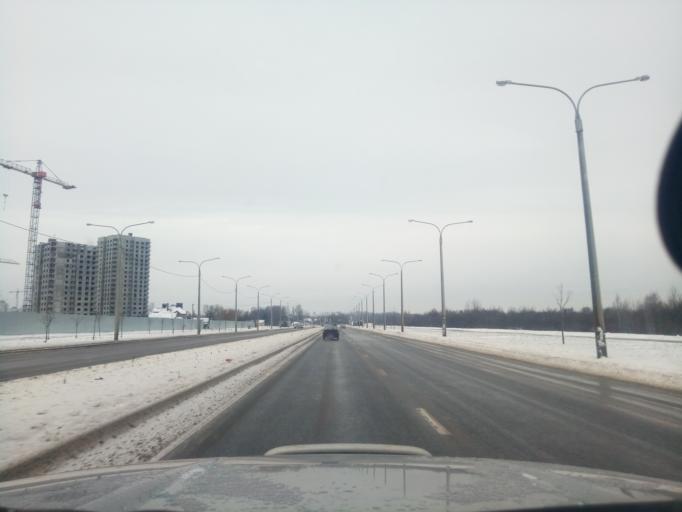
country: BY
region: Minsk
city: Machulishchy
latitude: 53.8381
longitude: 27.5968
